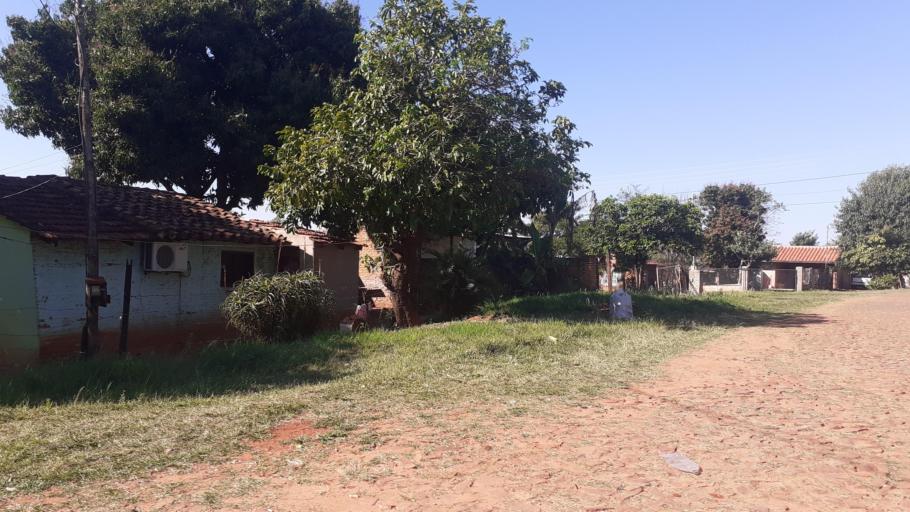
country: PY
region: Misiones
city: San Juan Bautista
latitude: -26.6672
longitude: -57.1247
